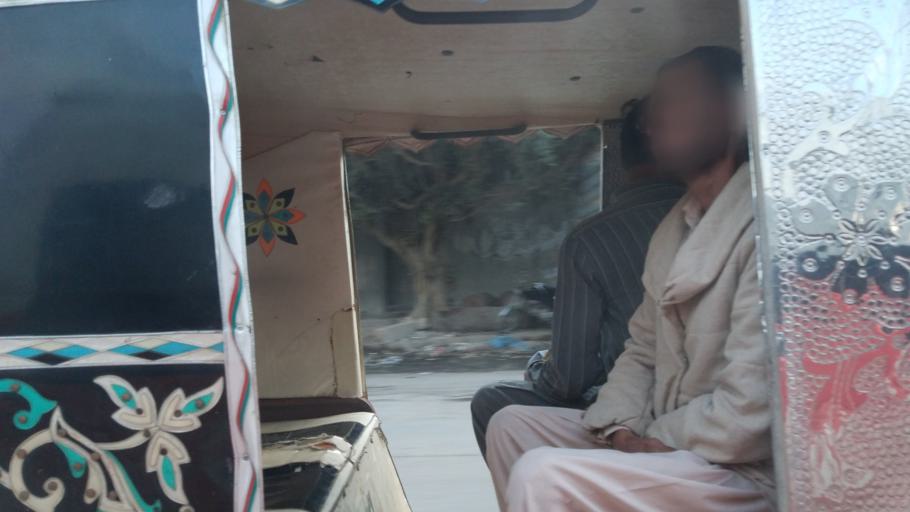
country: PK
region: Sindh
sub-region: Karachi District
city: Karachi
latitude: 24.9366
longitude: 67.0855
